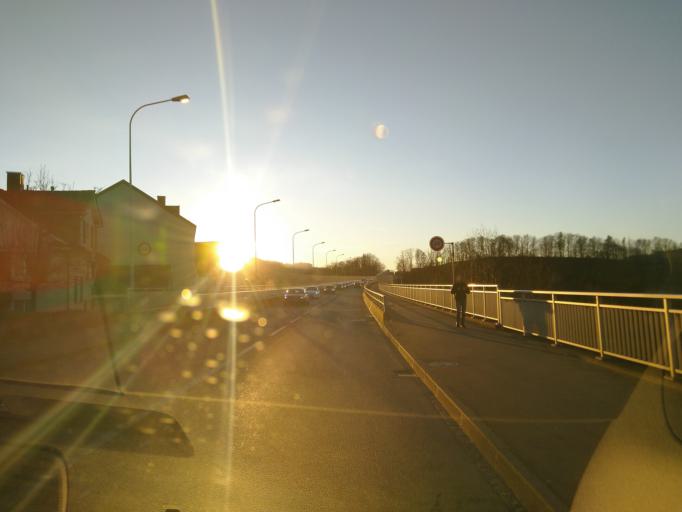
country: CH
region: Saint Gallen
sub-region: Wahlkreis St. Gallen
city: Sankt Gallen
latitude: 47.4076
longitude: 9.3265
